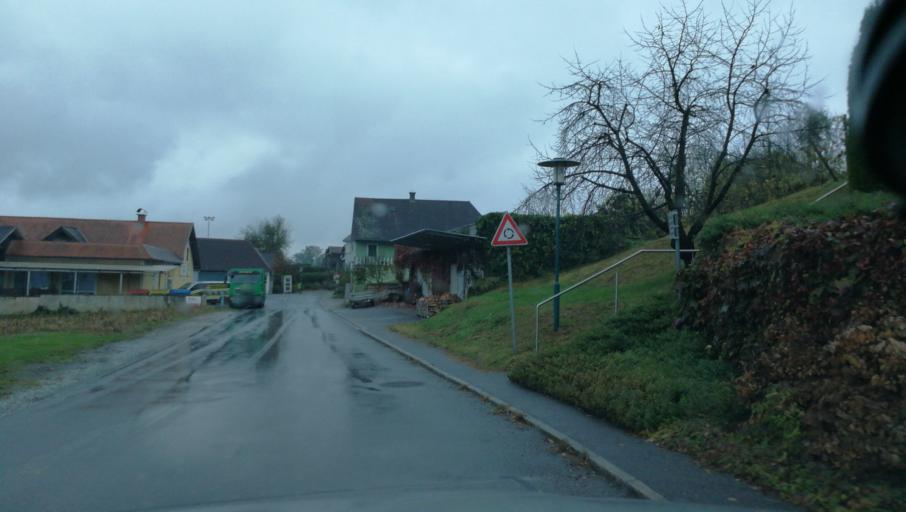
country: AT
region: Styria
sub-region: Politischer Bezirk Leibnitz
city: Sankt Veit am Vogau
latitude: 46.7481
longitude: 15.6280
